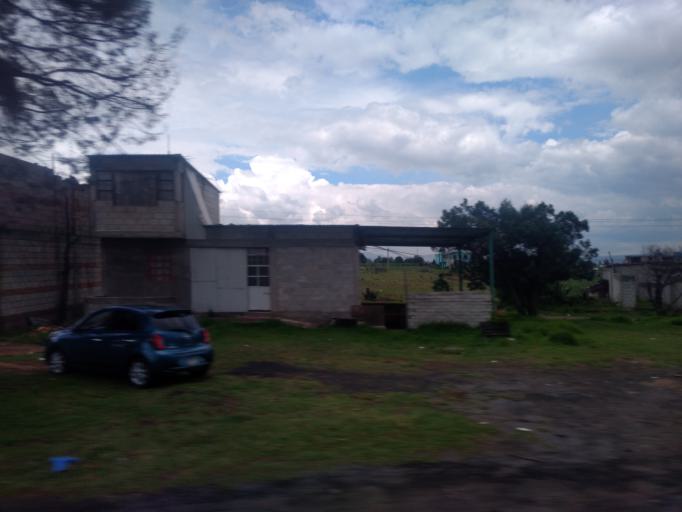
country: MX
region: Tlaxcala
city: Seccion Primera Santiago Tetla
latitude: 19.4425
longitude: -98.1291
